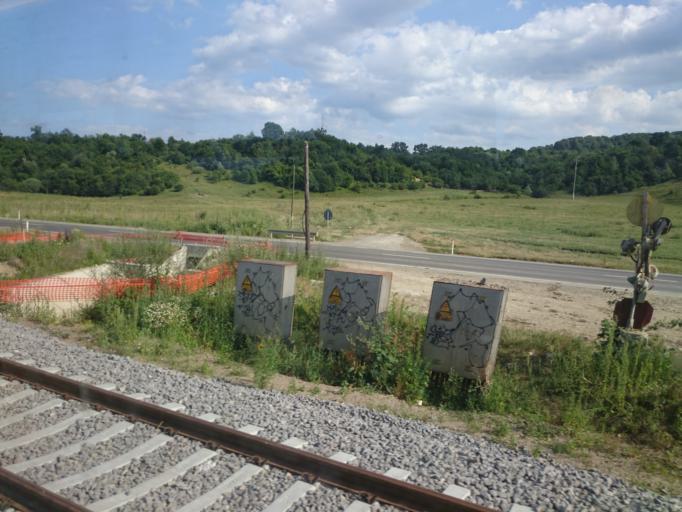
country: RO
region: Sibiu
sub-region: Comuna Hoghilag
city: Hoghilag
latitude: 46.2202
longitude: 24.6195
